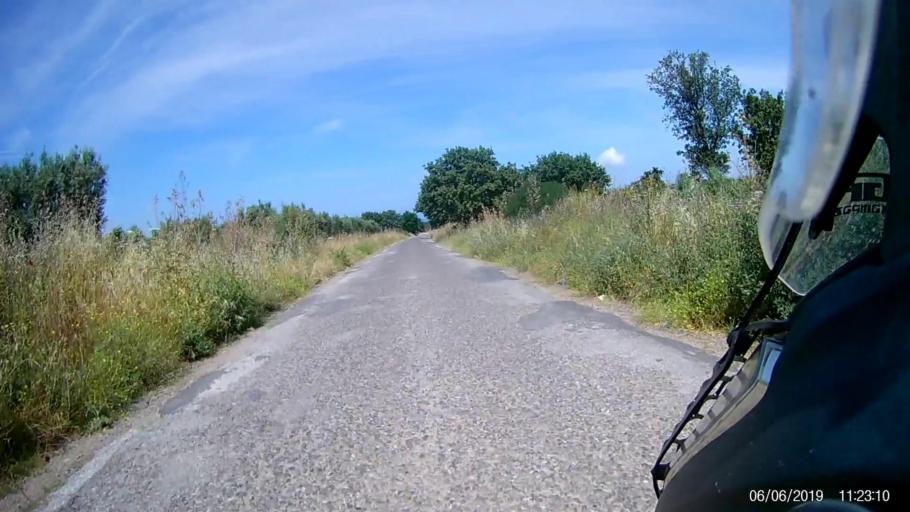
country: TR
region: Canakkale
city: Gulpinar
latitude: 39.6127
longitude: 26.1798
